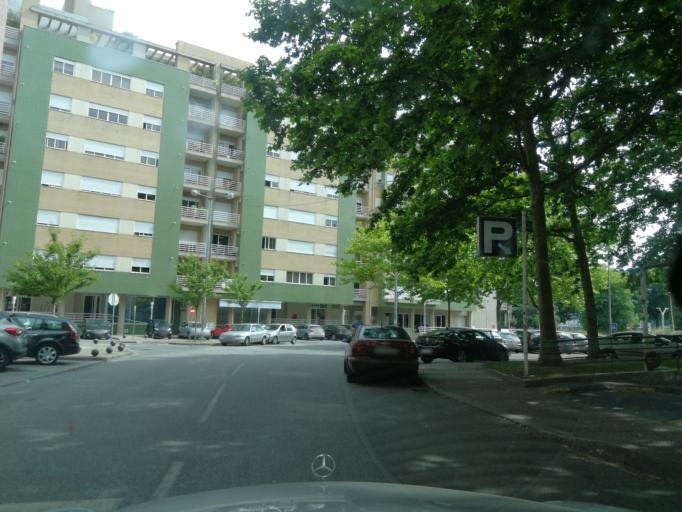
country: PT
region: Braga
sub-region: Vila Nova de Famalicao
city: Vila Nova de Famalicao
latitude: 41.4047
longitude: -8.5204
